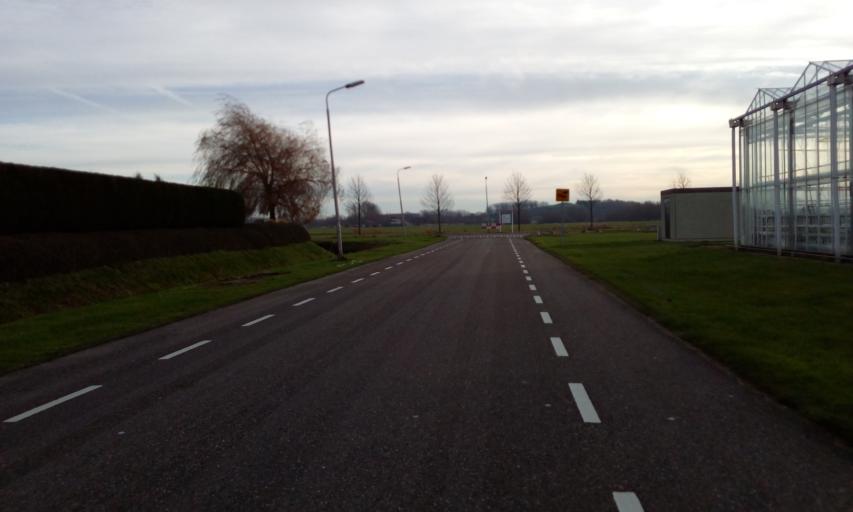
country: NL
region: South Holland
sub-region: Gemeente Lansingerland
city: Bleiswijk
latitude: 51.9849
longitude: 4.5346
